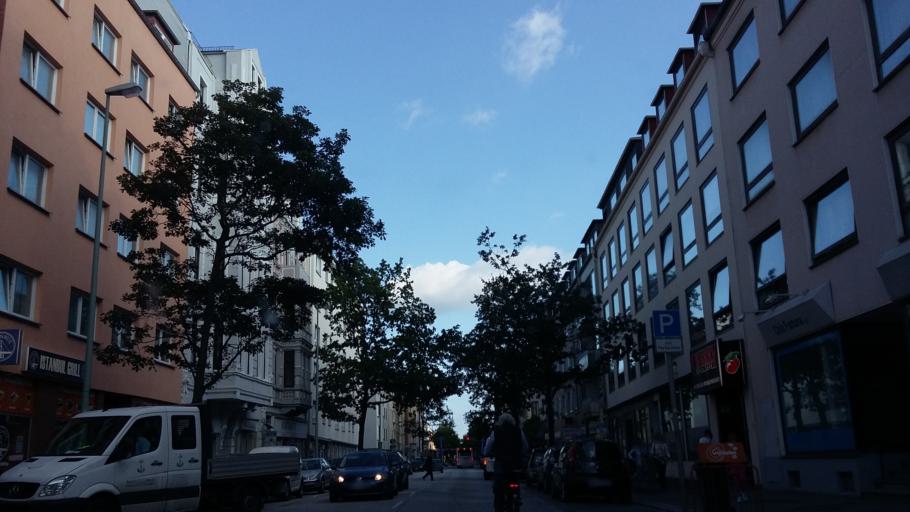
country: DE
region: Bremen
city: Bremerhaven
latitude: 53.5495
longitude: 8.5734
